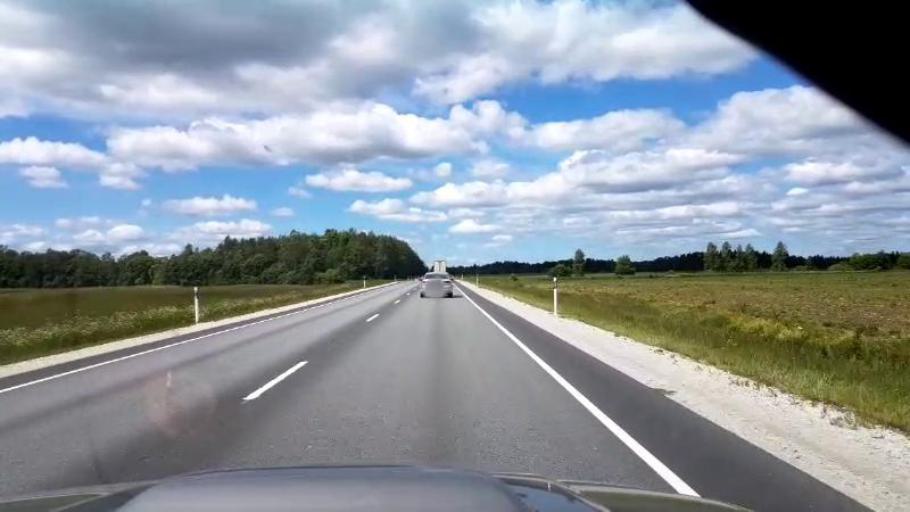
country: EE
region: Paernumaa
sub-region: Halinga vald
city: Parnu-Jaagupi
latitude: 58.6629
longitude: 24.4639
